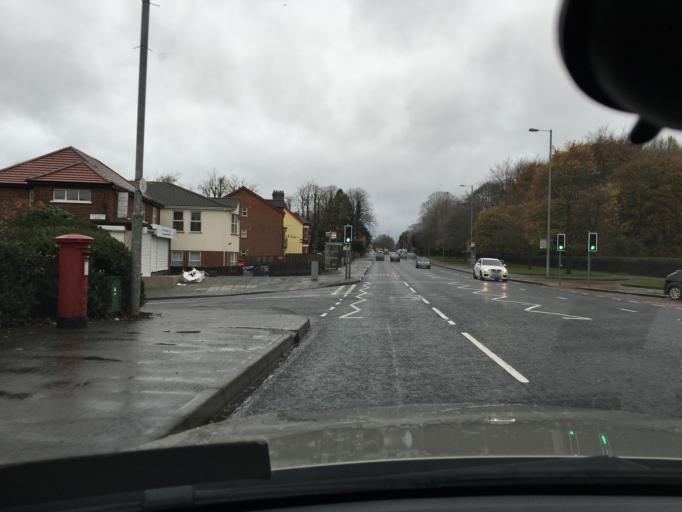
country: GB
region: Northern Ireland
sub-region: Castlereagh District
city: Dundonald
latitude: 54.5946
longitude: -5.8408
